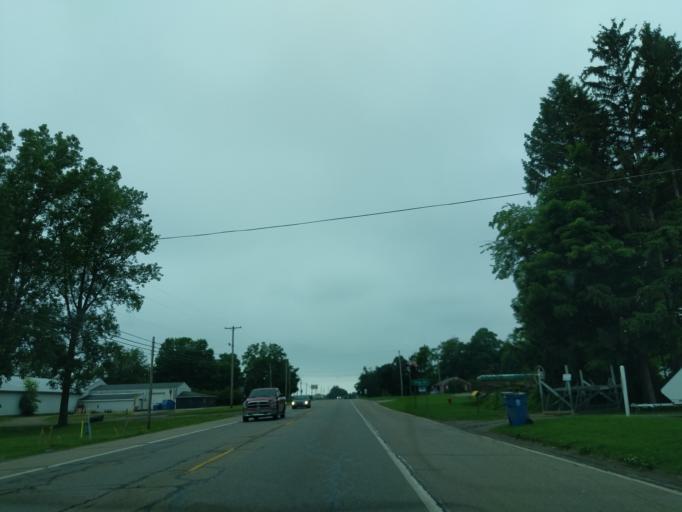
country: US
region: Michigan
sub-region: Branch County
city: Quincy
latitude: 41.9400
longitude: -84.9102
